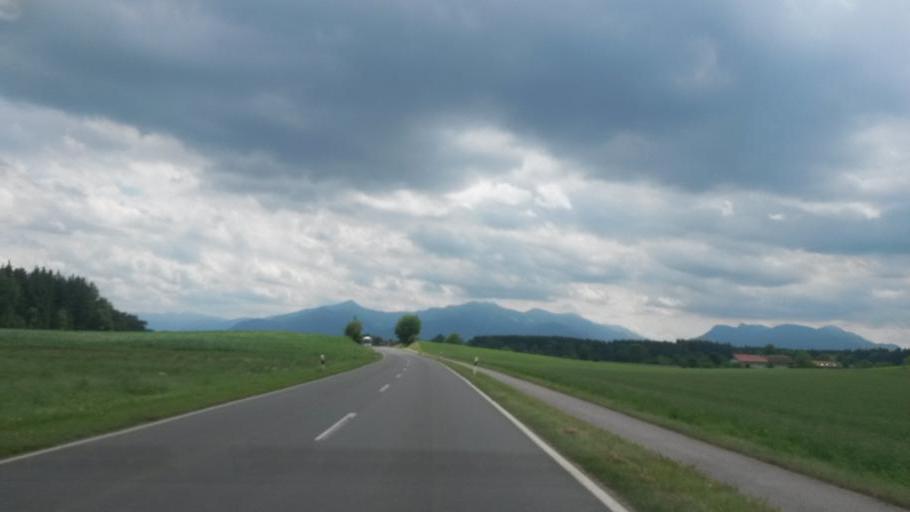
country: DE
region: Bavaria
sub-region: Upper Bavaria
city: Eggstatt
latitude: 47.9039
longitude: 12.3911
